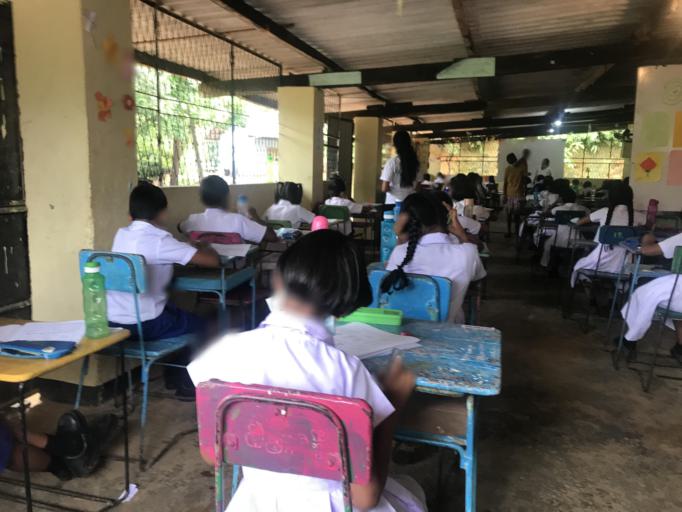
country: LK
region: Sabaragamuwa
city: Ratnapura
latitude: 6.4485
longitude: 80.5121
